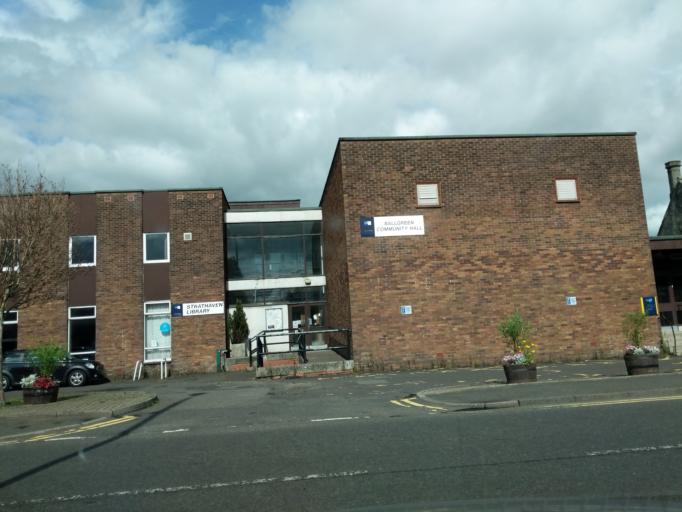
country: GB
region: Scotland
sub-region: South Lanarkshire
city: Strathaven
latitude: 55.6802
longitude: -4.0676
